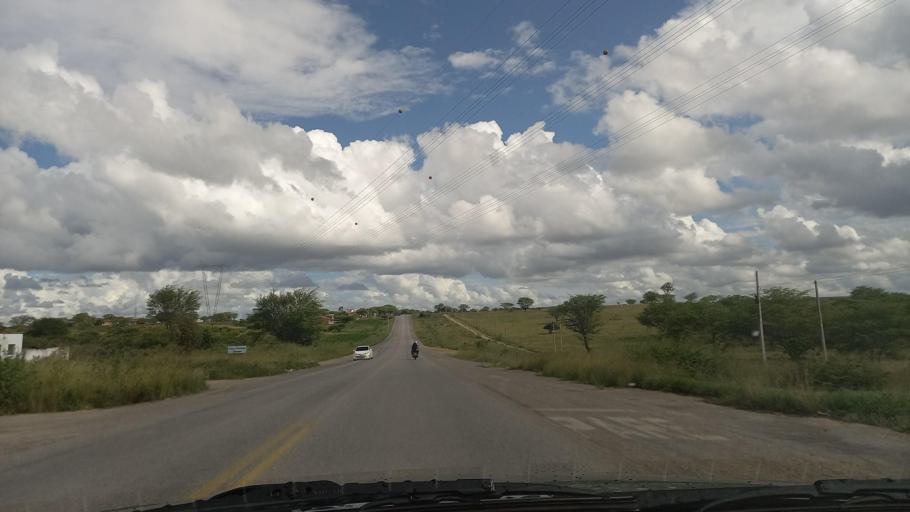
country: BR
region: Pernambuco
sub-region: Lajedo
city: Lajedo
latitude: -8.6016
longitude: -36.2925
